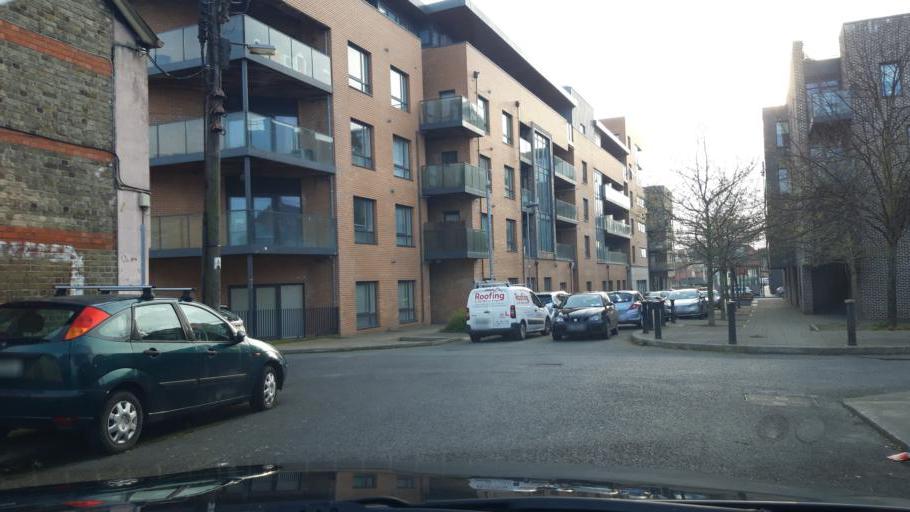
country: IE
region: Leinster
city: Rialto
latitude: 53.3378
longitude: -6.2914
